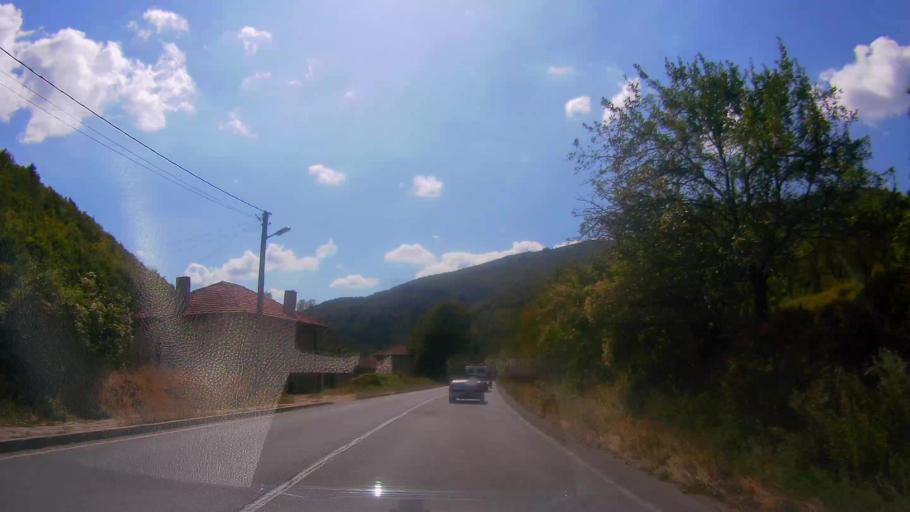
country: BG
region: Stara Zagora
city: Gurkovo
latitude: 42.7418
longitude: 25.7089
